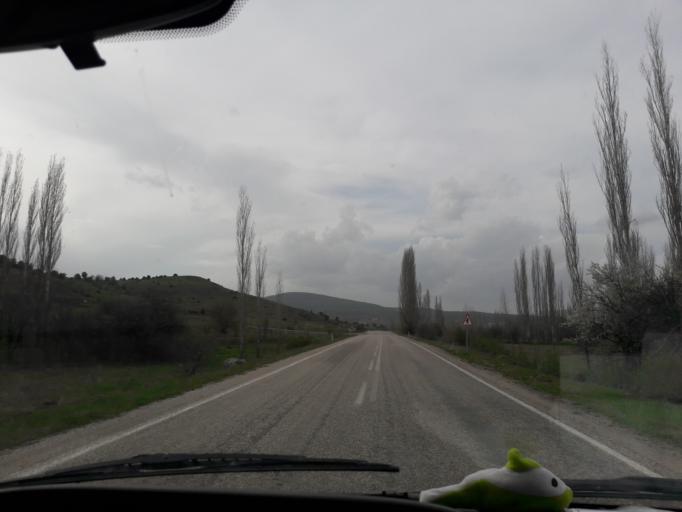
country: TR
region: Gumushane
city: Siran
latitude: 40.1666
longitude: 39.0058
